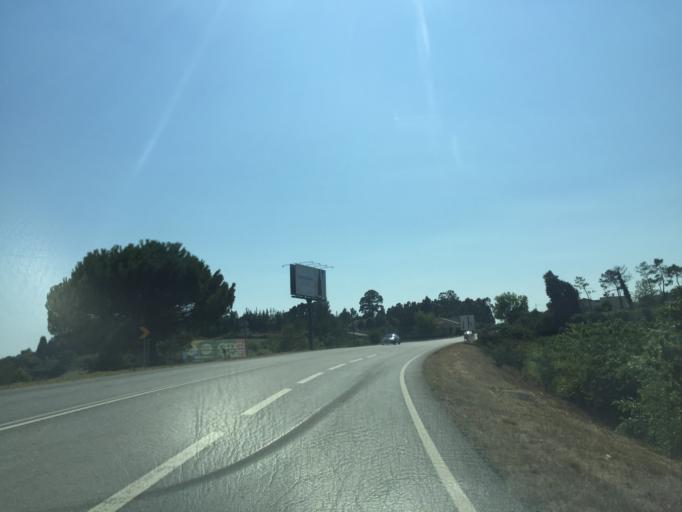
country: PT
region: Aveiro
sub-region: Mealhada
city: Mealhada
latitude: 40.3662
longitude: -8.4914
